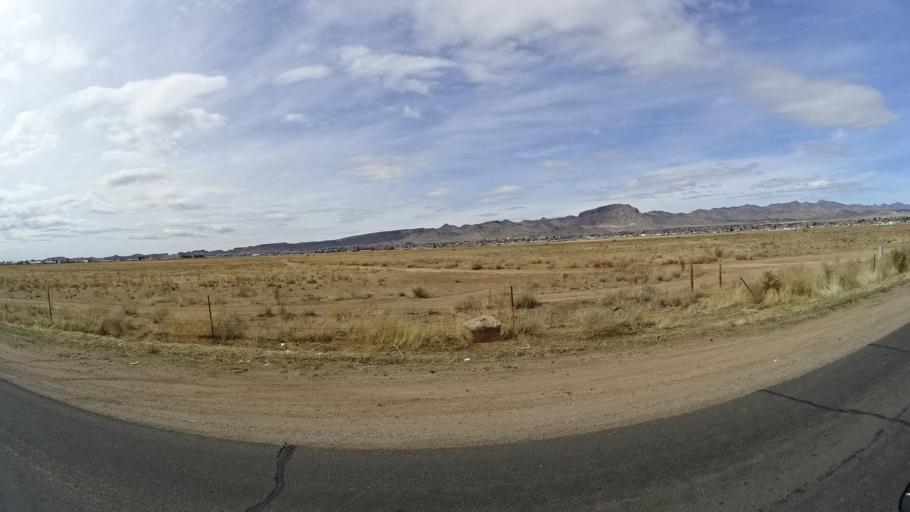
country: US
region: Arizona
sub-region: Mohave County
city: New Kingman-Butler
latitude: 35.2447
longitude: -113.9952
